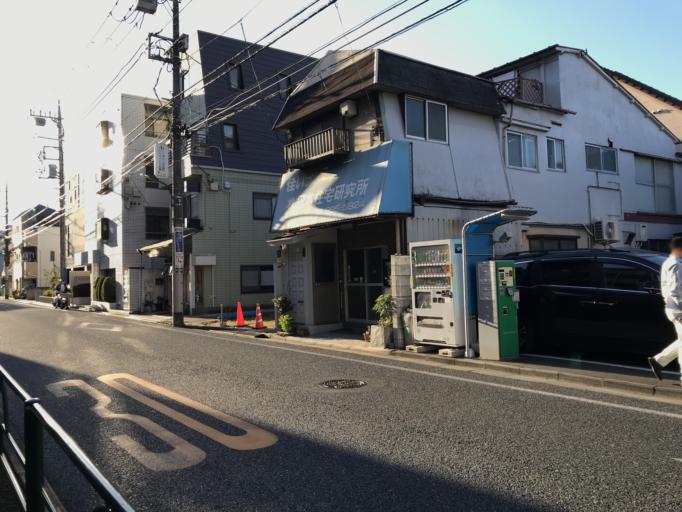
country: JP
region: Saitama
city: Wako
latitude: 35.7429
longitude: 139.5993
